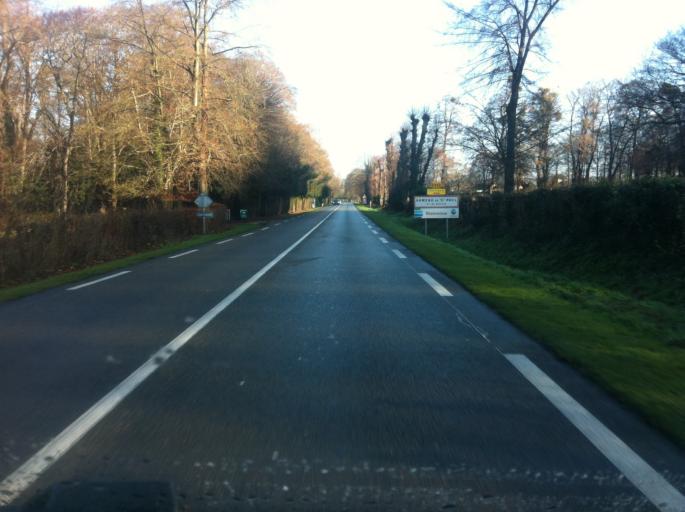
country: FR
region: Haute-Normandie
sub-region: Departement de la Seine-Maritime
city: Yainville
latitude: 49.4659
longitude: 0.8518
